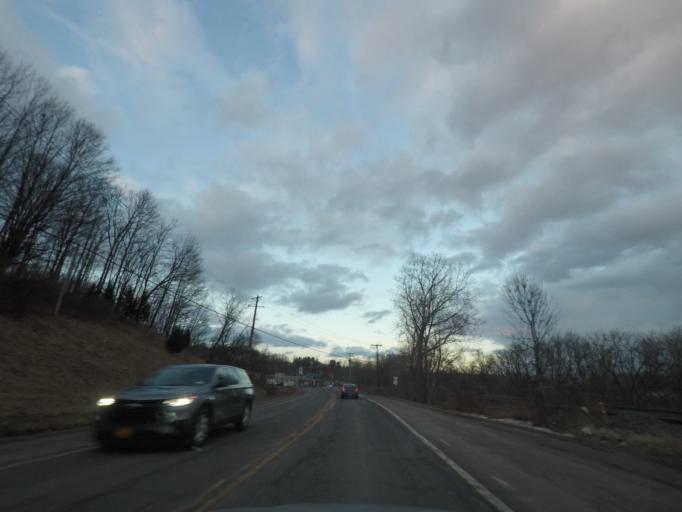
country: US
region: New York
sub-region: Montgomery County
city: Fonda
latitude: 42.9528
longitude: -74.3823
